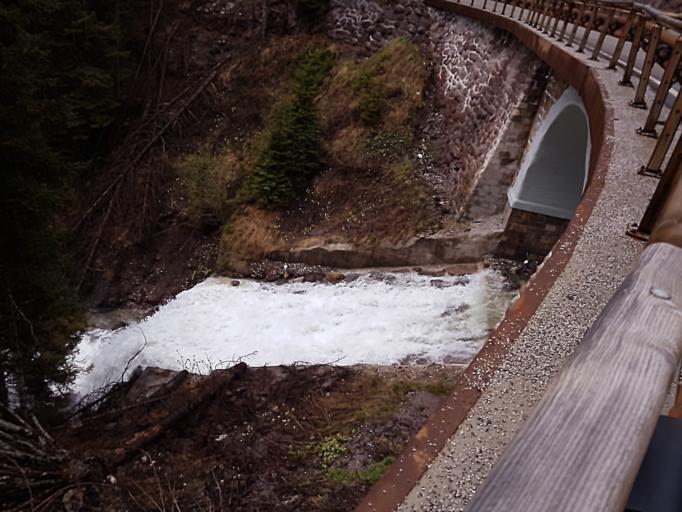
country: AT
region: Tyrol
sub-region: Politischer Bezirk Lienz
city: Kartitsch
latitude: 46.6538
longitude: 12.4411
